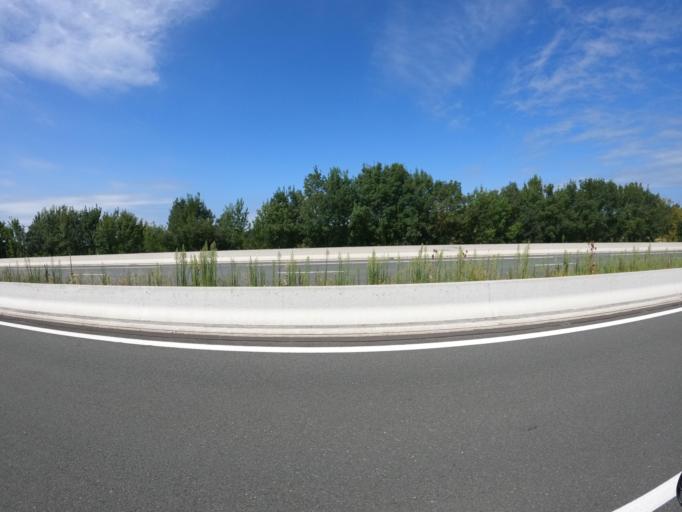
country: FR
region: Poitou-Charentes
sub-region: Departement des Deux-Sevres
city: Frontenay-Rohan-Rohan
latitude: 46.2323
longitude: -0.5870
